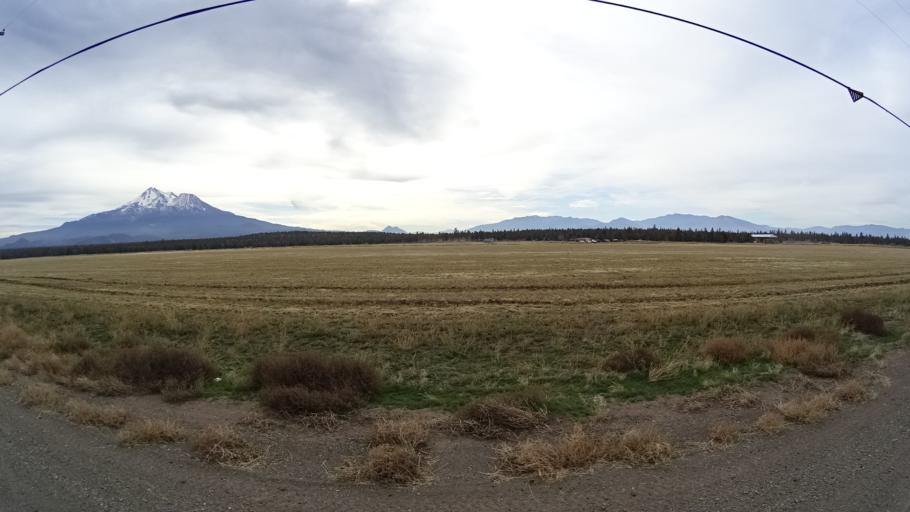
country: US
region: California
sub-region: Siskiyou County
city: Weed
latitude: 41.5961
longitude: -122.3354
